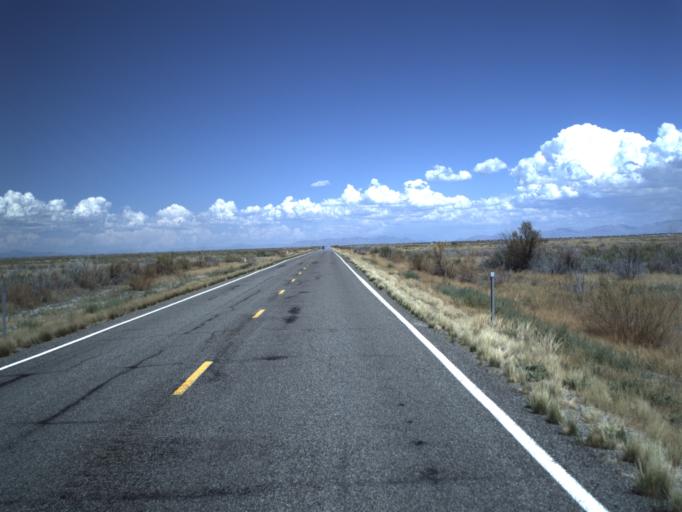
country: US
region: Utah
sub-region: Millard County
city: Delta
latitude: 39.2896
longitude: -112.8299
